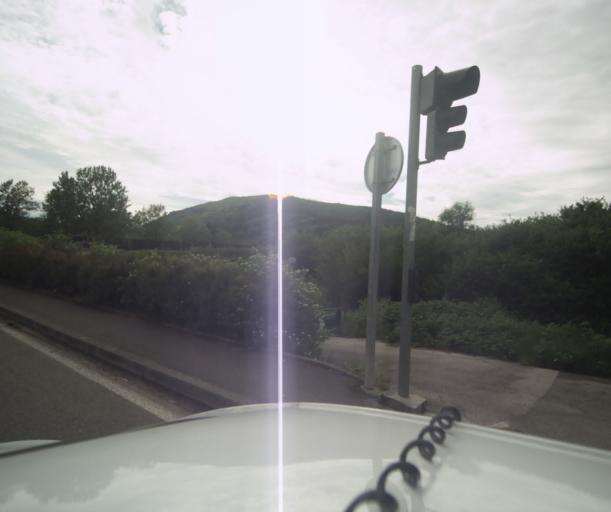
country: FR
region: Franche-Comte
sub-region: Departement du Doubs
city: Beure
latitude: 47.2106
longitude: 6.0010
